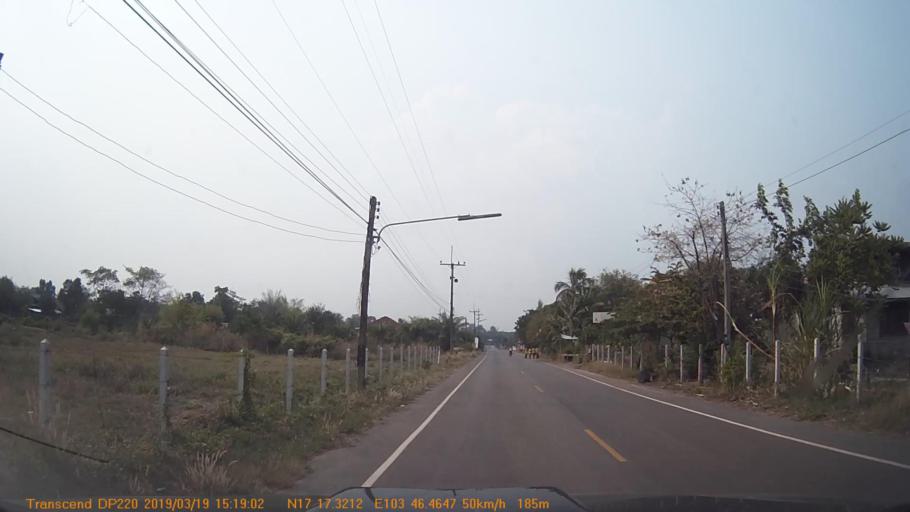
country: TH
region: Sakon Nakhon
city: Phanna Nikhom
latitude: 17.2889
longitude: 103.7743
